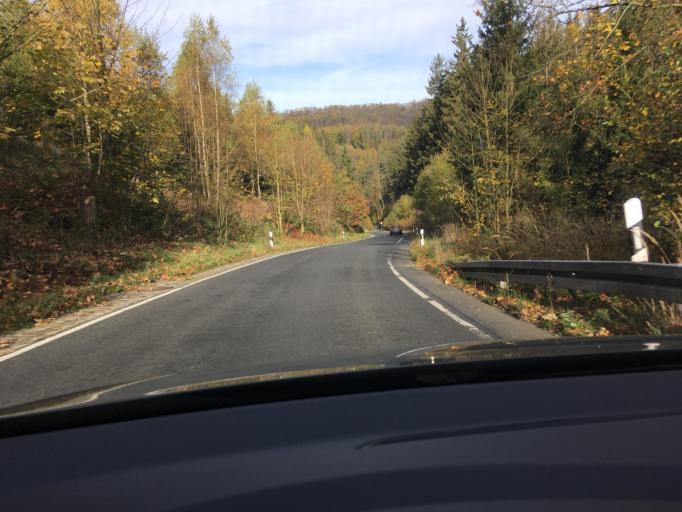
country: DE
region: Saxony
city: Glashutte
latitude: 50.8499
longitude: 13.7957
